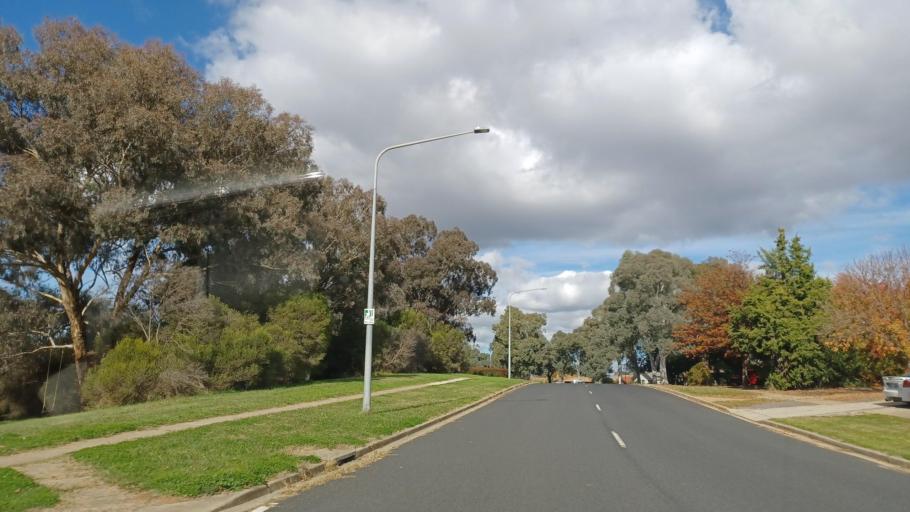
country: AU
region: Australian Capital Territory
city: Belconnen
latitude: -35.2064
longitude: 149.0703
